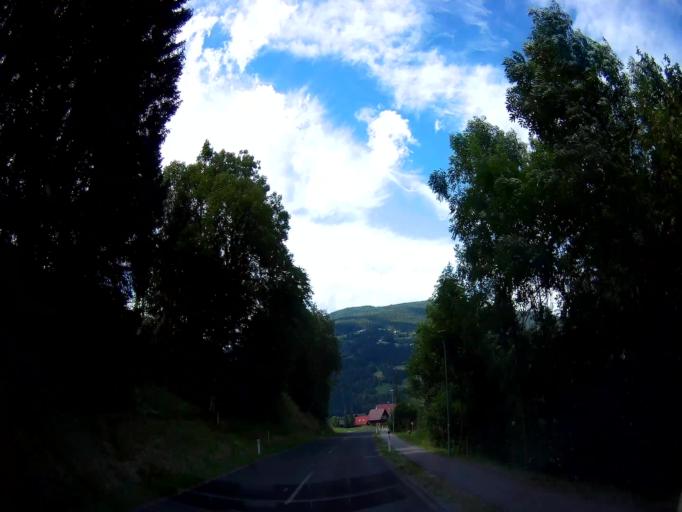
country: AT
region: Styria
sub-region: Politischer Bezirk Murau
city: Stadl an der Mur
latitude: 47.0755
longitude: 13.9832
